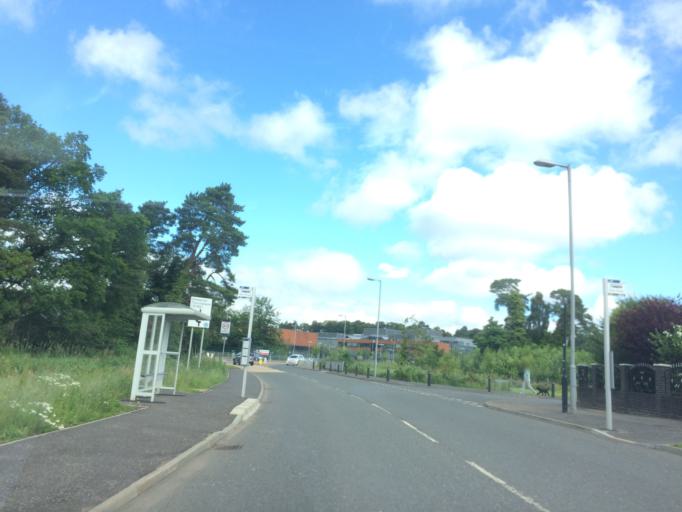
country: GB
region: Scotland
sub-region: East Renfrewshire
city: Newton Mearns
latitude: 55.7844
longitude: -4.3279
